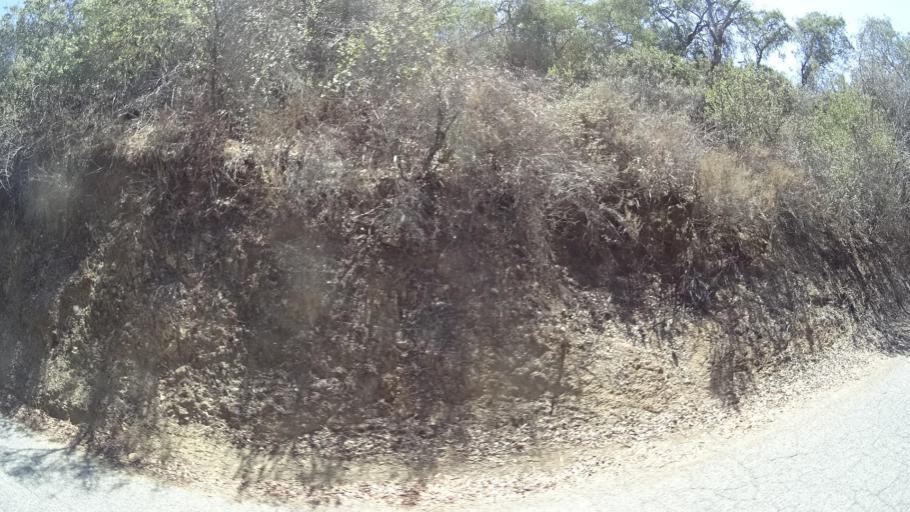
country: US
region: California
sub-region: San Diego County
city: Rainbow
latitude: 33.3889
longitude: -117.0403
